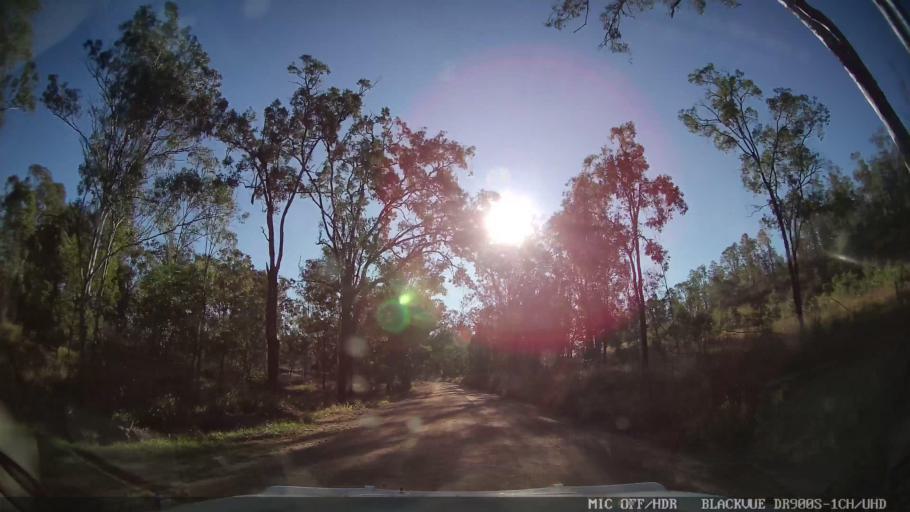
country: AU
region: Queensland
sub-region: Bundaberg
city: Sharon
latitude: -24.7923
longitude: 151.6128
